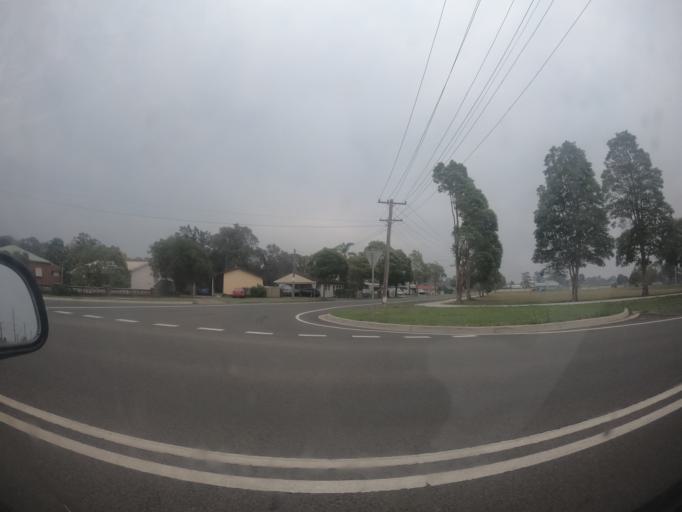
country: AU
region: New South Wales
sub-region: Shellharbour
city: Albion Park Rail
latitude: -34.5691
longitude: 150.7944
